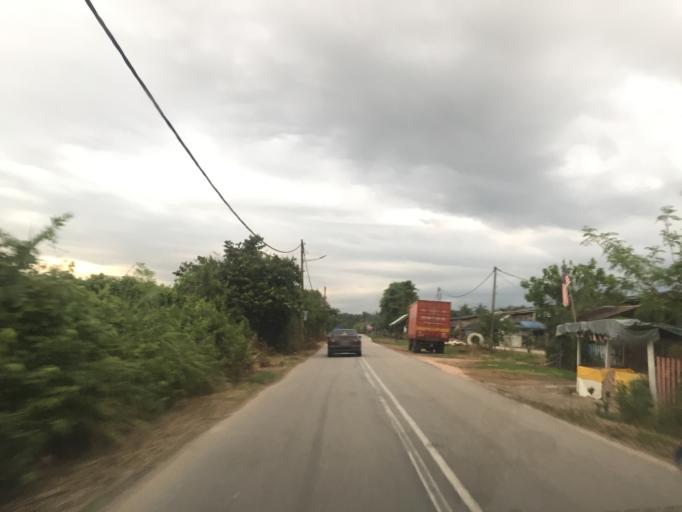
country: MY
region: Penang
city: Tasek Glugor
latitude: 5.5407
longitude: 100.5225
